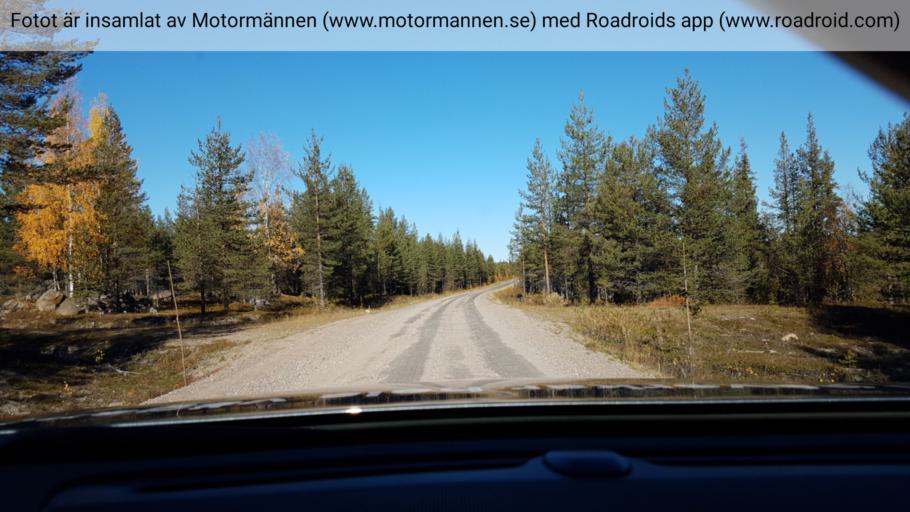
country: SE
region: Norrbotten
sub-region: Gallivare Kommun
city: Gaellivare
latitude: 66.6194
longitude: 21.0232
